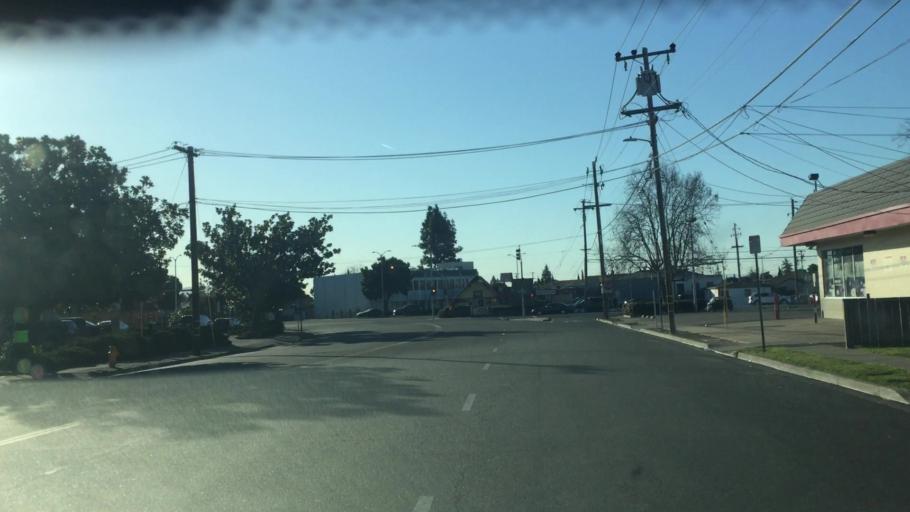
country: US
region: California
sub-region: Alameda County
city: Hayward
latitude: 37.6637
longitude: -122.0851
